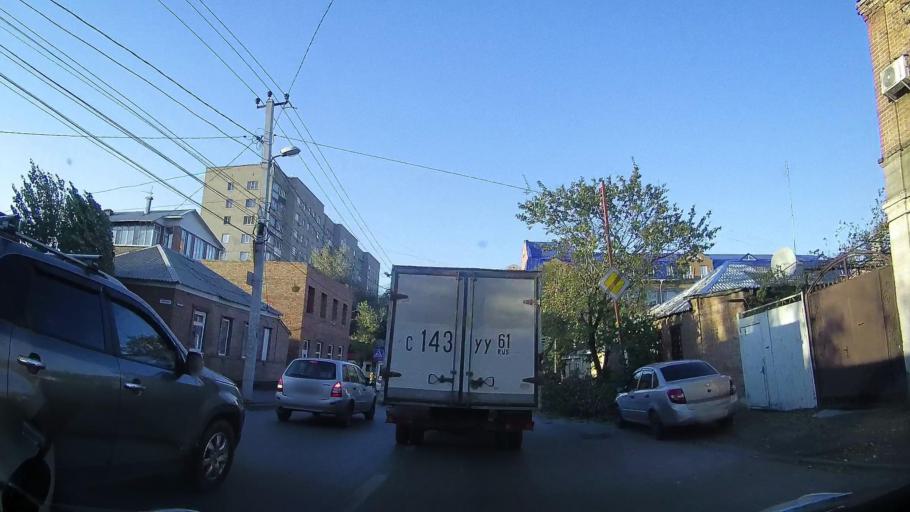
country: RU
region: Rostov
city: Rostov-na-Donu
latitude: 47.2316
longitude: 39.6927
